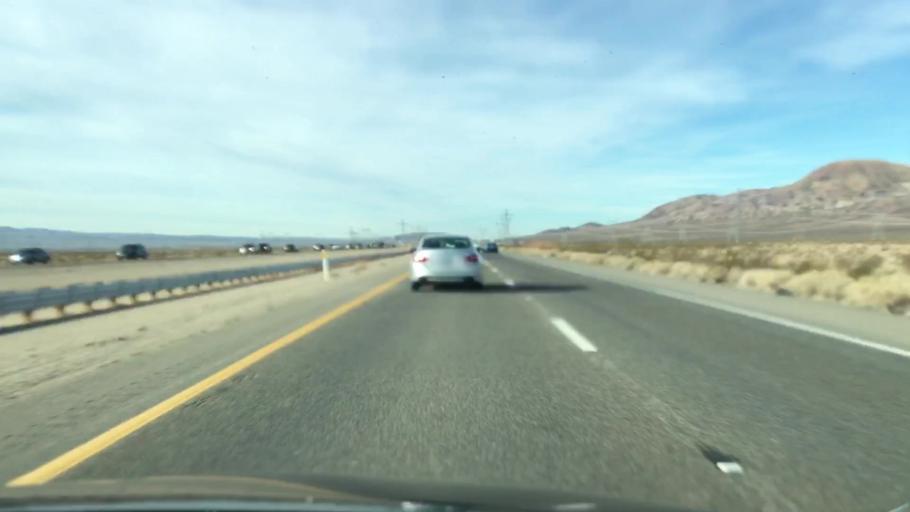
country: US
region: California
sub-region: San Bernardino County
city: Barstow
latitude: 34.9248
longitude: -116.7398
